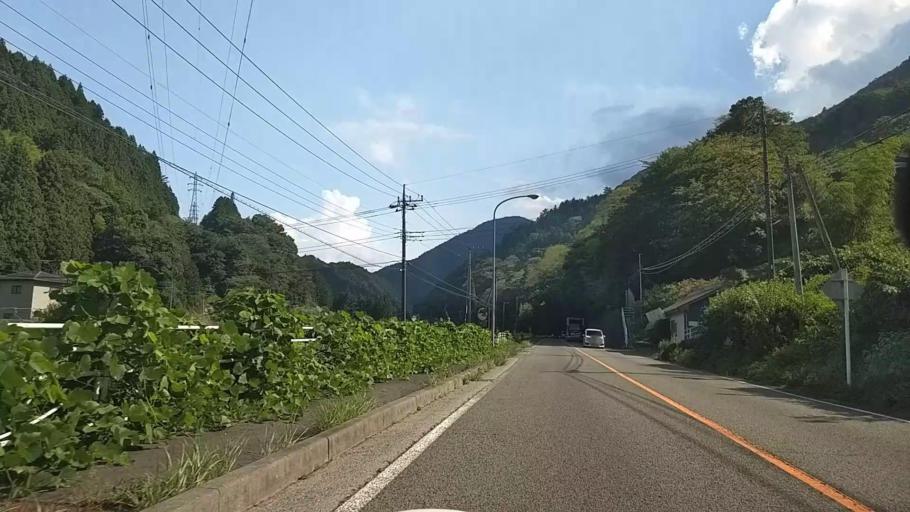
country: JP
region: Shizuoka
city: Fujinomiya
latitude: 35.3394
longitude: 138.4244
